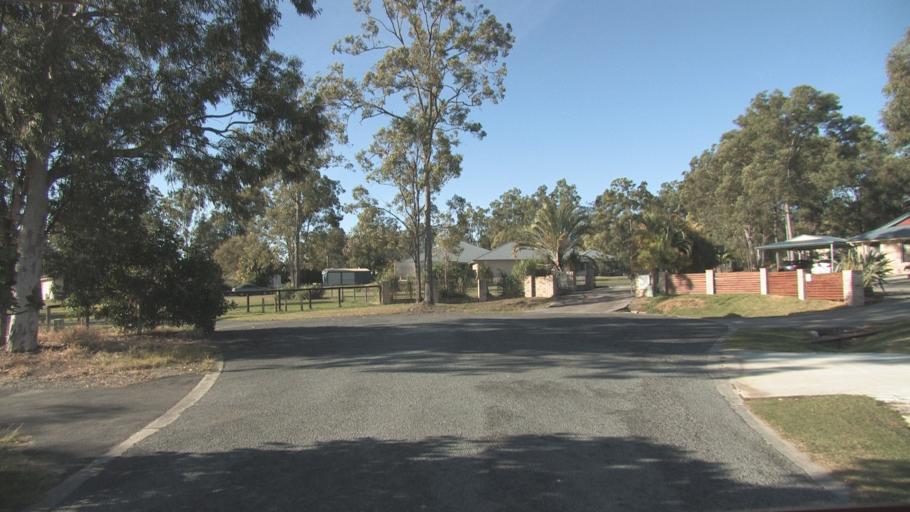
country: AU
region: Queensland
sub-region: Logan
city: North Maclean
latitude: -27.7396
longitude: 152.9572
